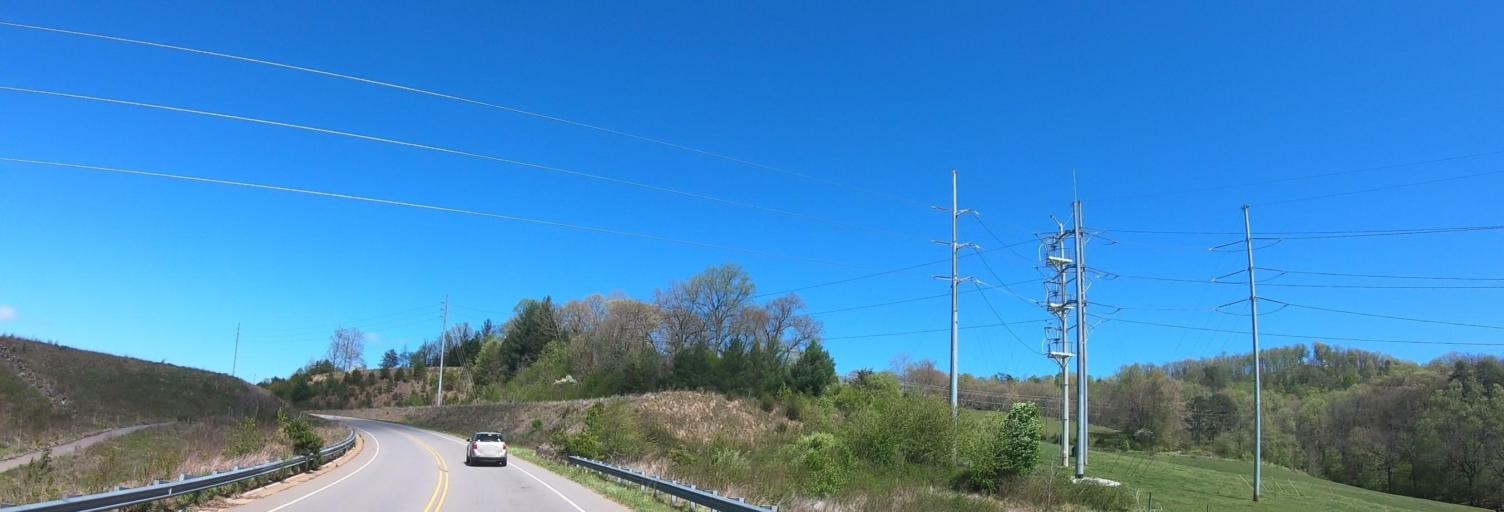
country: US
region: North Carolina
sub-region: Macon County
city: Franklin
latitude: 35.1615
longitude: -83.3734
